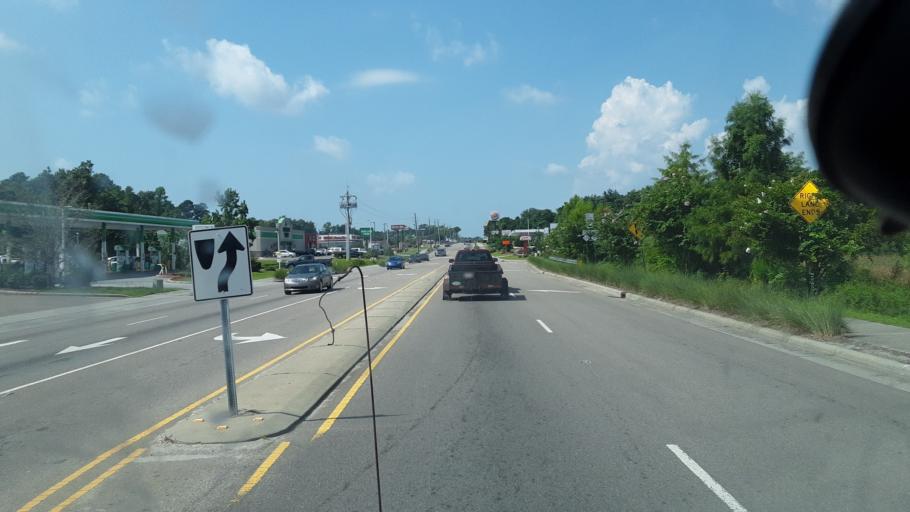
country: US
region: North Carolina
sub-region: Brunswick County
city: Shallotte
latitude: 33.9793
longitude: -78.3767
